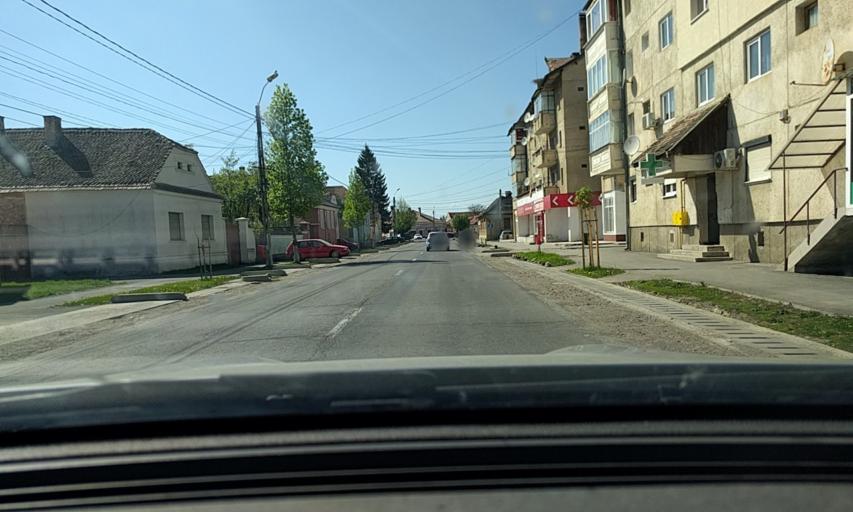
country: RO
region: Brasov
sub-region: Comuna Prejmer
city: Prejmer
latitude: 45.7189
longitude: 25.7749
